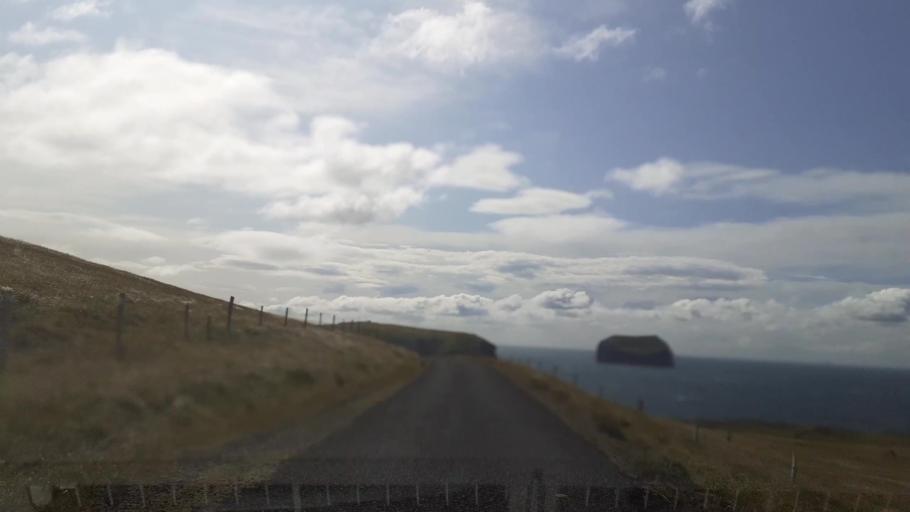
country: IS
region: South
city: Vestmannaeyjar
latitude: 63.4189
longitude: -20.2809
